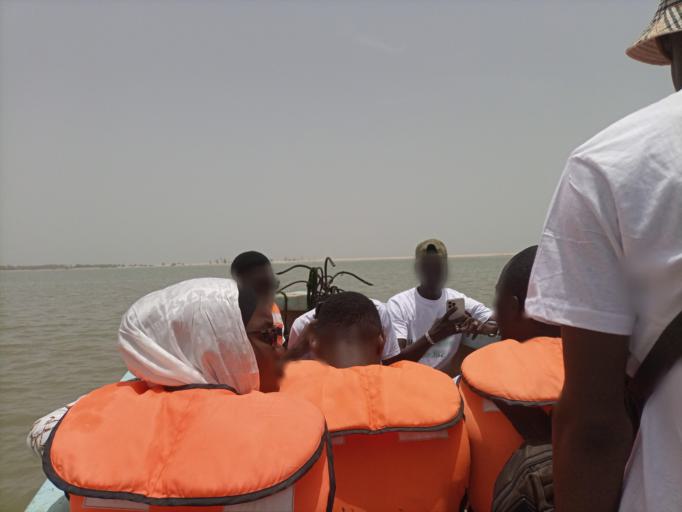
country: SN
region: Saint-Louis
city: Saint-Louis
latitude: 15.8647
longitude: -16.5136
